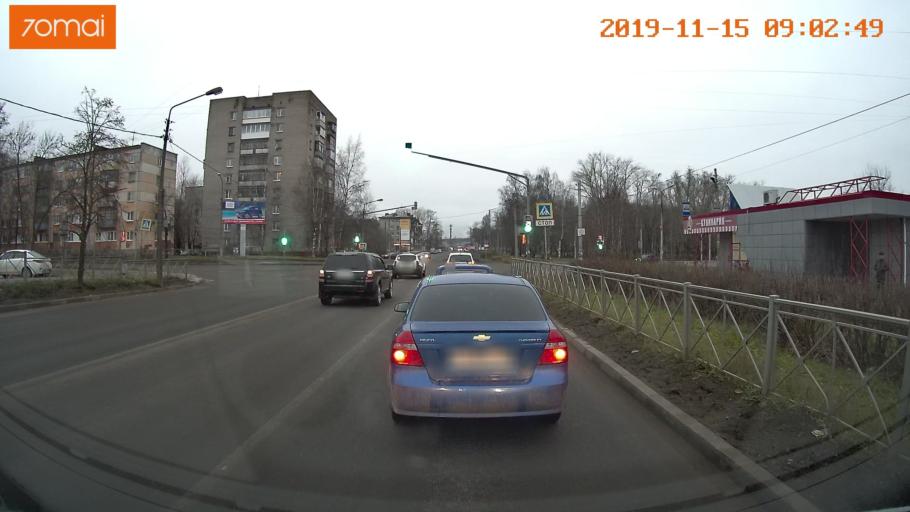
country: RU
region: Vologda
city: Cherepovets
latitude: 59.1368
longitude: 37.9259
